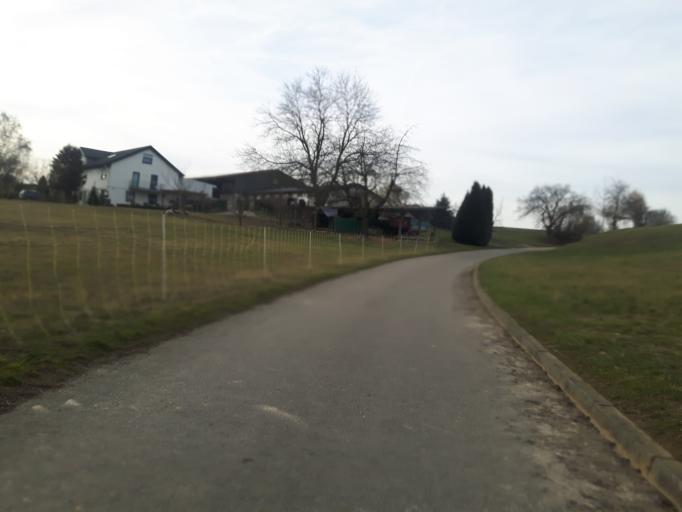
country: DE
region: Baden-Wuerttemberg
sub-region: Regierungsbezirk Stuttgart
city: Bretzfeld
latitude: 49.1922
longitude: 9.4388
